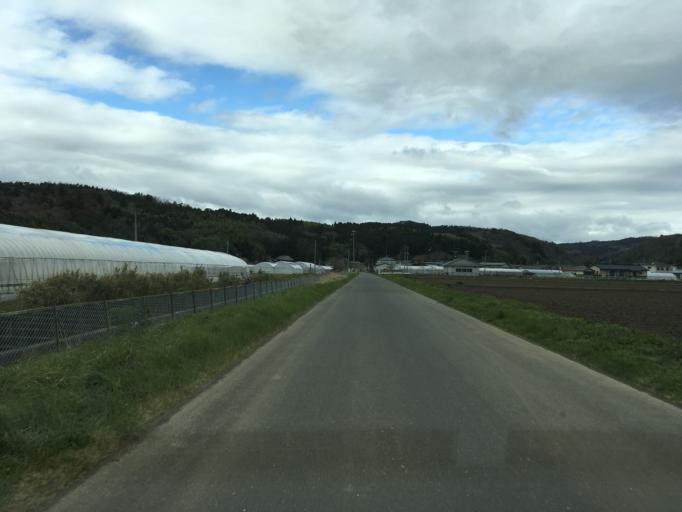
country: JP
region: Iwate
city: Ichinoseki
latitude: 38.7585
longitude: 141.2663
